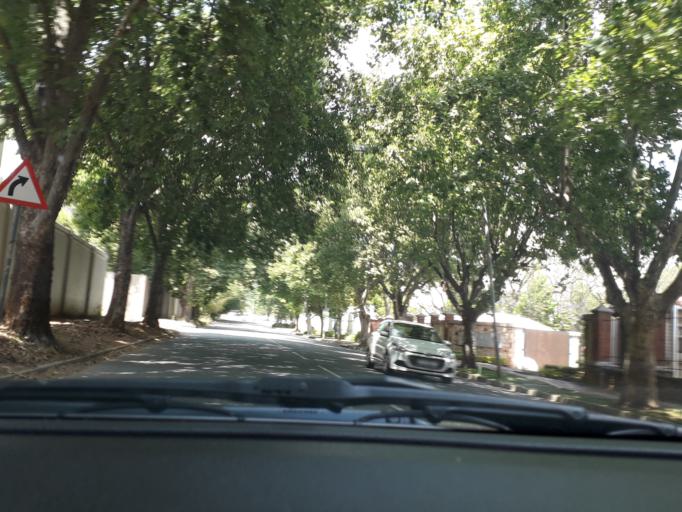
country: ZA
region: Gauteng
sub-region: City of Johannesburg Metropolitan Municipality
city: Johannesburg
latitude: -26.1604
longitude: 28.0584
